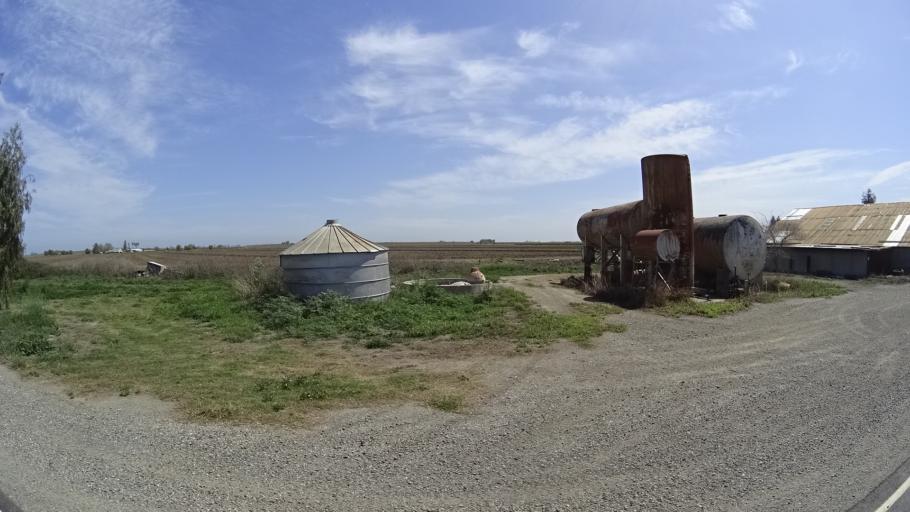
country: US
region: California
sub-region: Glenn County
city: Hamilton City
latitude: 39.6173
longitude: -122.0650
